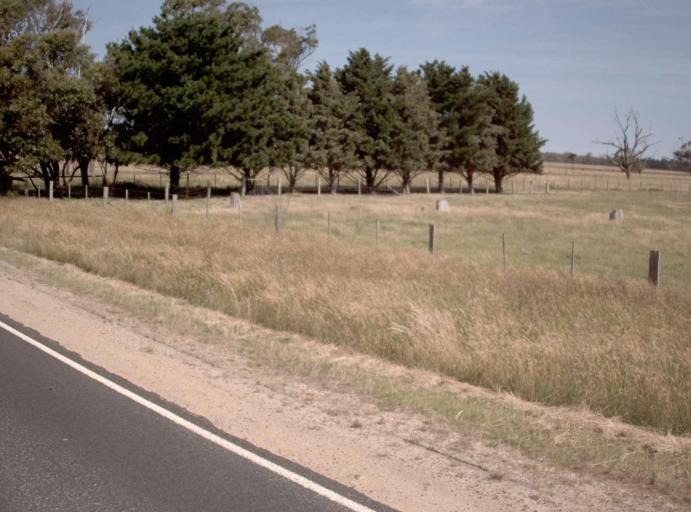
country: AU
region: Victoria
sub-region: Wellington
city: Sale
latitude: -38.2176
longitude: 147.1411
